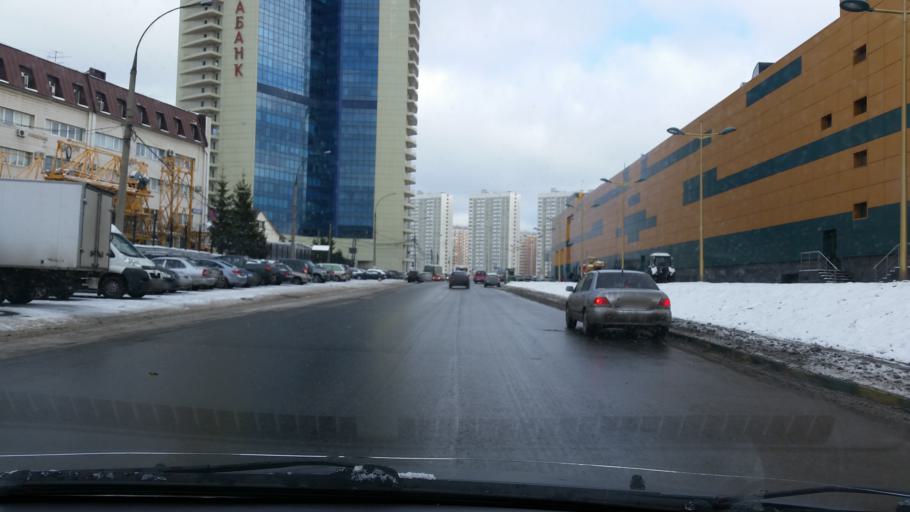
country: RU
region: Moscow
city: Vagonoremont
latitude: 55.9102
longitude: 37.5402
